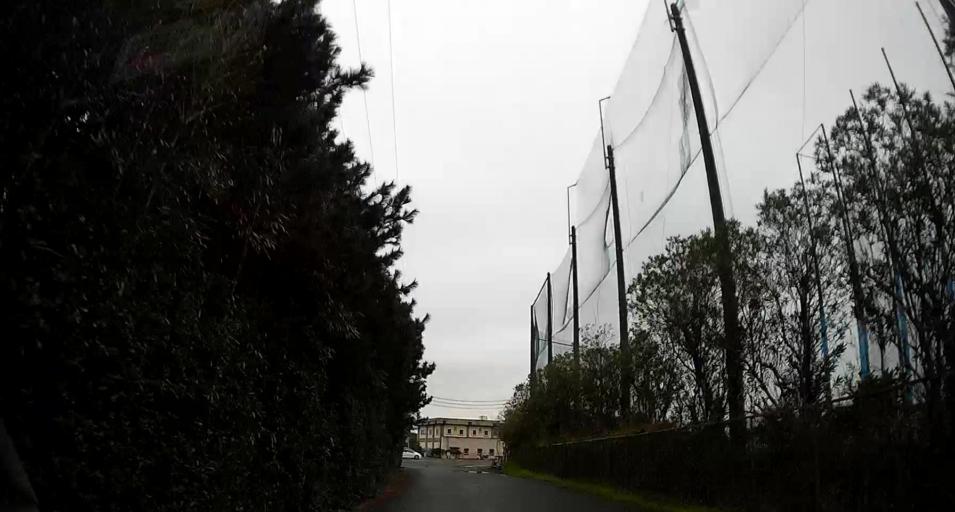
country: JP
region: Chiba
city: Kisarazu
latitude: 35.4067
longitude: 139.9031
